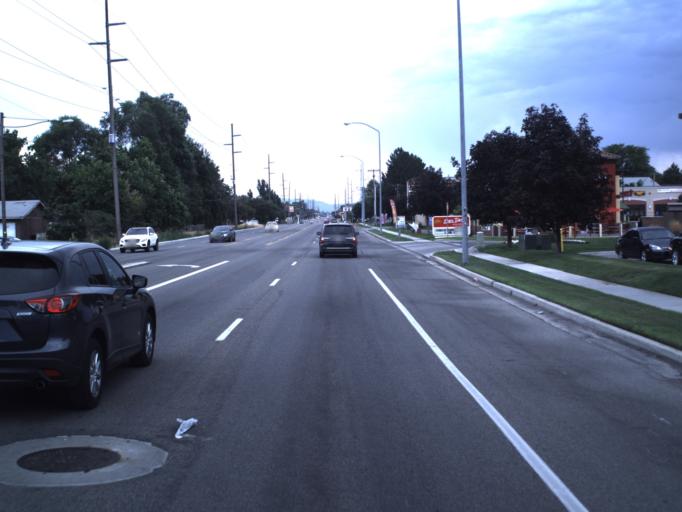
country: US
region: Utah
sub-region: Salt Lake County
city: Murray
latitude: 40.6483
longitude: -111.8660
